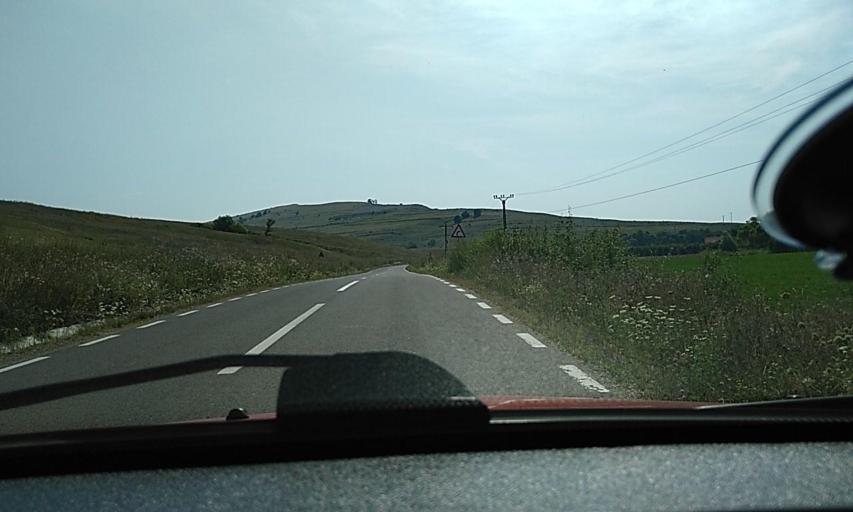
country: RO
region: Brasov
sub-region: Oras Rupea
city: Fiser
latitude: 46.0395
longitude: 25.1280
